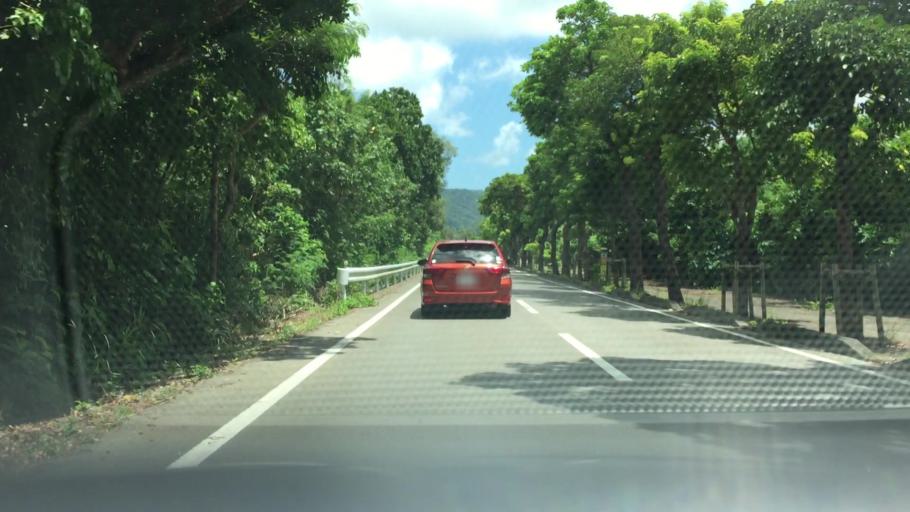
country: JP
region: Okinawa
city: Ishigaki
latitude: 24.3899
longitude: 124.1408
